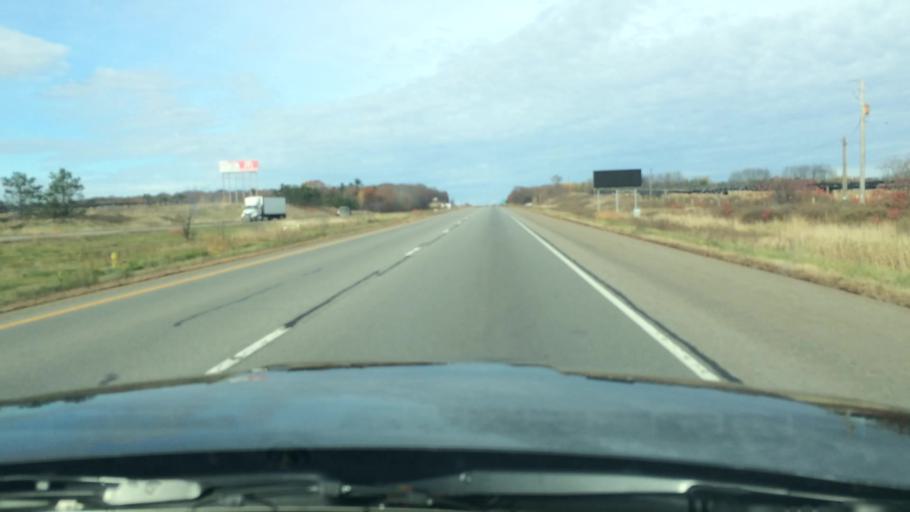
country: US
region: Wisconsin
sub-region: Marathon County
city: Mosinee
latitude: 44.7568
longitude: -89.6798
